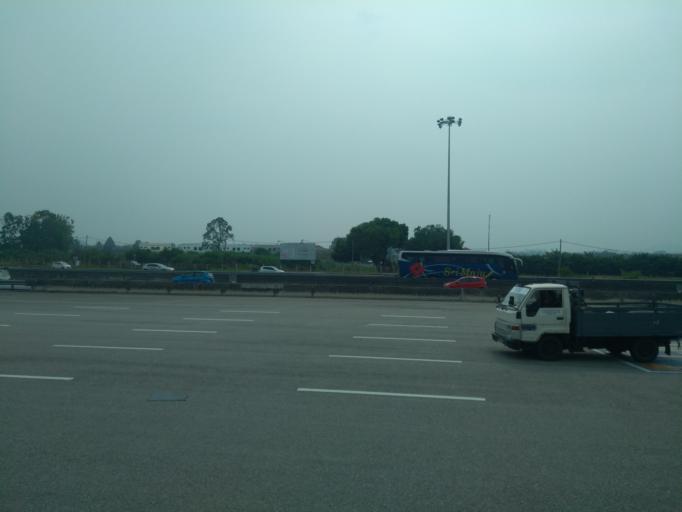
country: MY
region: Perak
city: Ipoh
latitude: 4.5861
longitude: 101.1449
